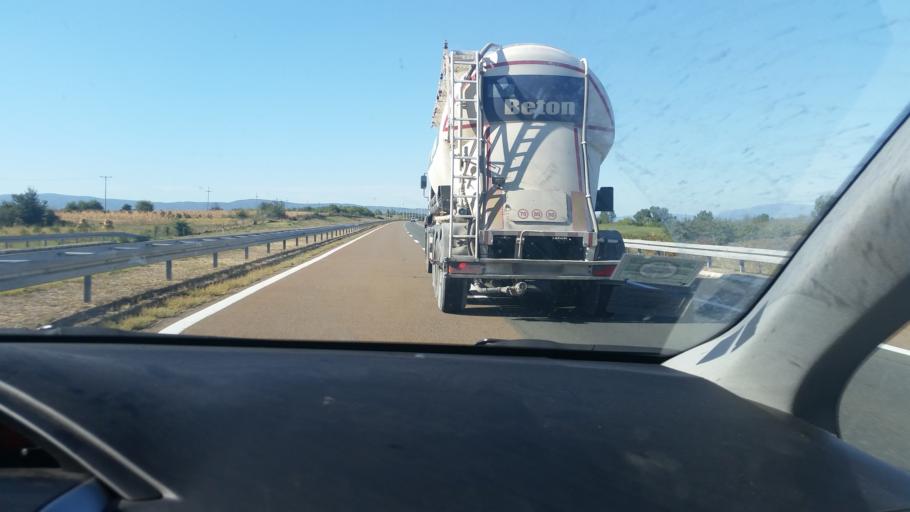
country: RS
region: Central Serbia
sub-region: Nisavski Okrug
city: Doljevac
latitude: 43.2729
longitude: 21.8059
